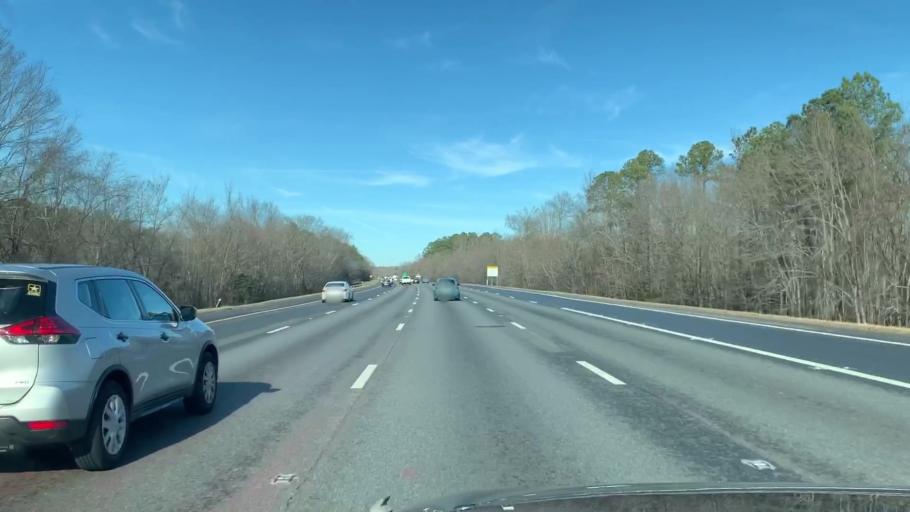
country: US
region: Virginia
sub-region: Henrico County
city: Highland Springs
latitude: 37.5544
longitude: -77.2891
